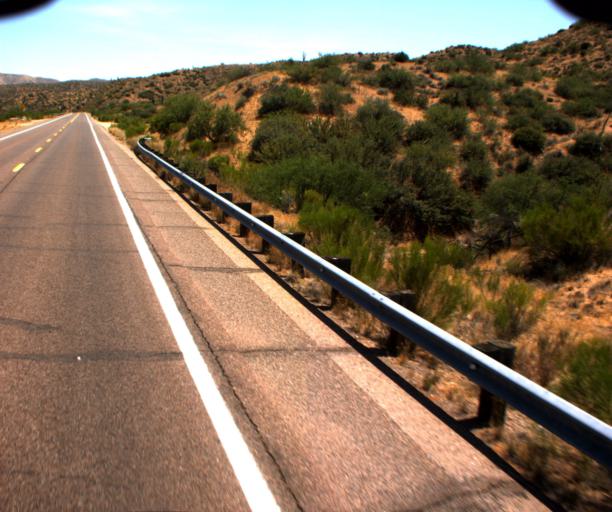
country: US
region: Arizona
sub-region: Gila County
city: Tonto Basin
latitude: 33.7716
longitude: -111.2601
